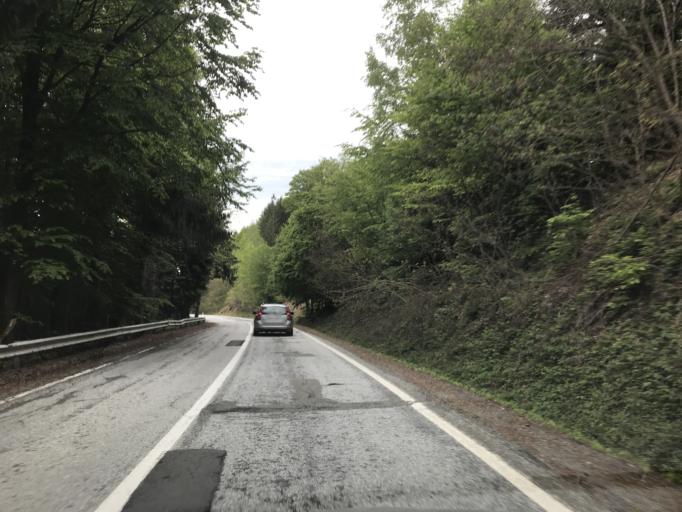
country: RO
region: Sibiu
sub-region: Comuna Cartisoara
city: Cartisoara
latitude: 45.6700
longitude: 24.5923
